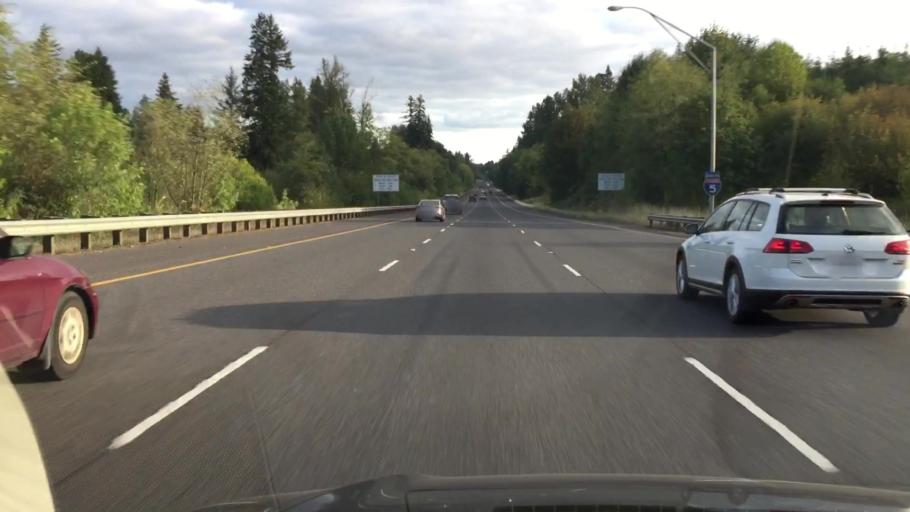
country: US
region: Washington
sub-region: Cowlitz County
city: Castle Rock
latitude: 46.2275
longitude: -122.8893
